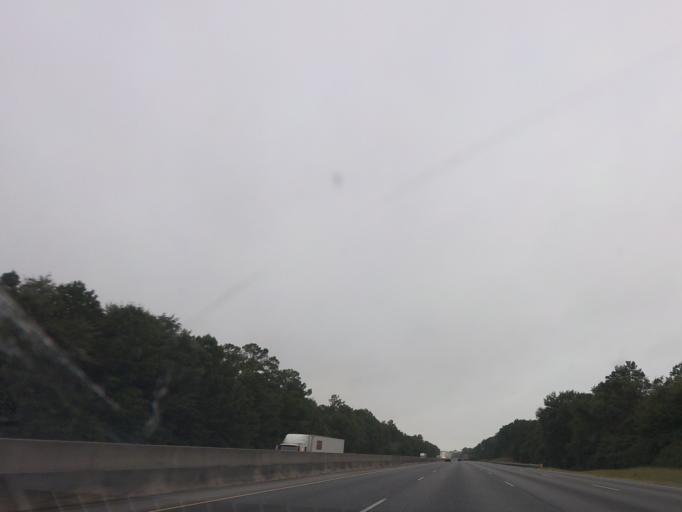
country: US
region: Georgia
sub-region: Monroe County
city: Forsyth
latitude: 33.0141
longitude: -83.8836
